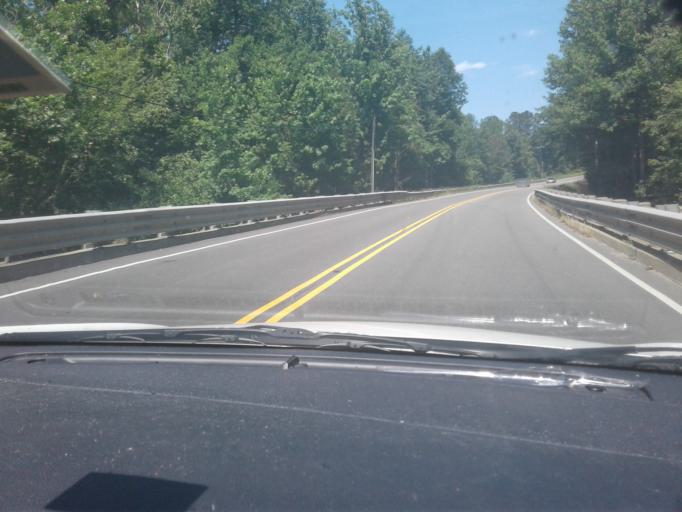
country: US
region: North Carolina
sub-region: Harnett County
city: Lillington
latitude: 35.4282
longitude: -78.8236
